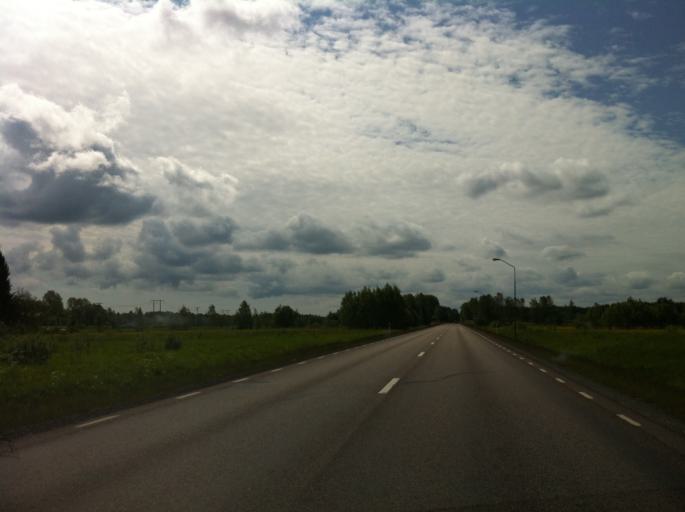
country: SE
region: Vaermland
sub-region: Karlstads Kommun
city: Edsvalla
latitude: 59.4760
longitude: 13.2160
